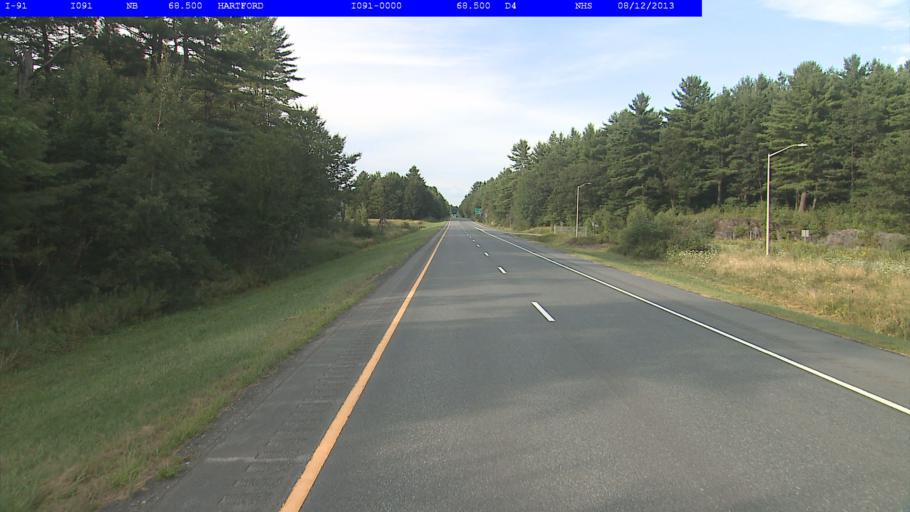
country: US
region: Vermont
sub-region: Windsor County
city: White River Junction
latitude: 43.6218
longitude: -72.3463
